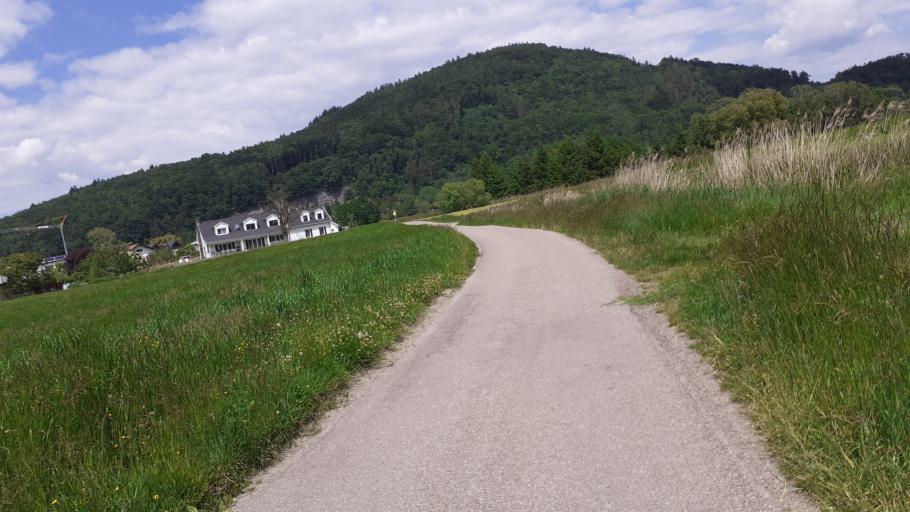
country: AT
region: Vorarlberg
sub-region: Politischer Bezirk Feldkirch
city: Koblach
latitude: 47.3250
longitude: 9.6108
